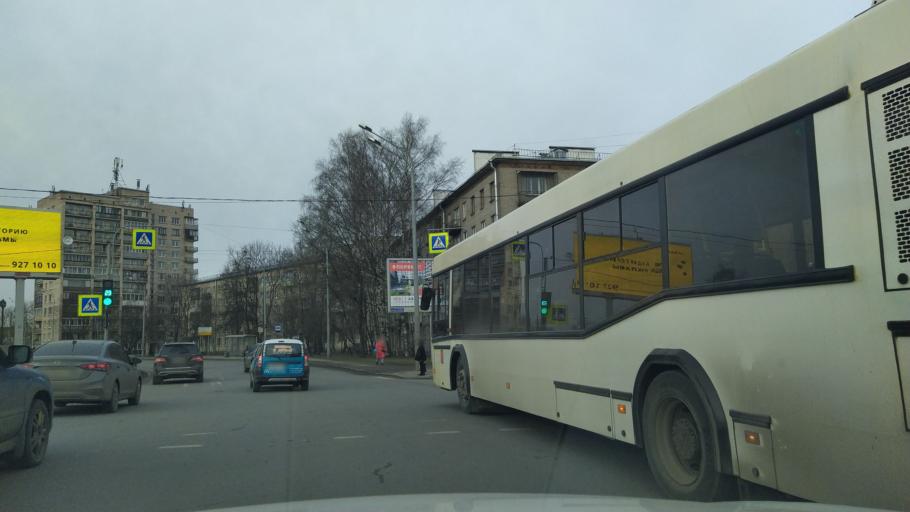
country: RU
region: Leningrad
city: Chernaya Rechka
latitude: 59.9896
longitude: 30.3017
